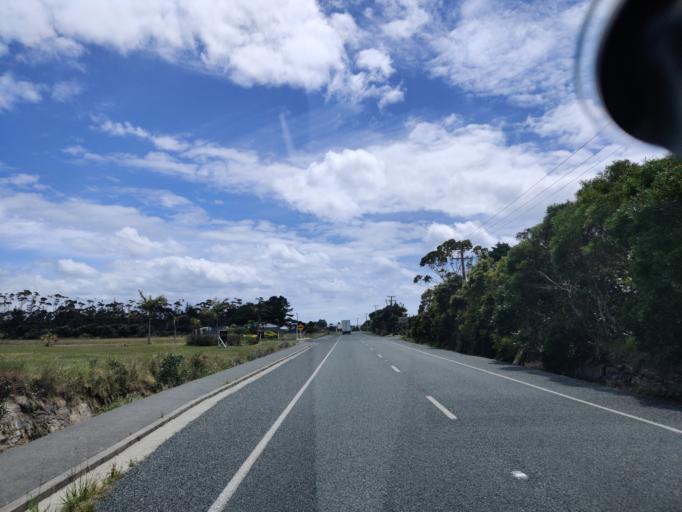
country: NZ
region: Northland
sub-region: Far North District
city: Kaitaia
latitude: -34.8267
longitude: 173.1280
